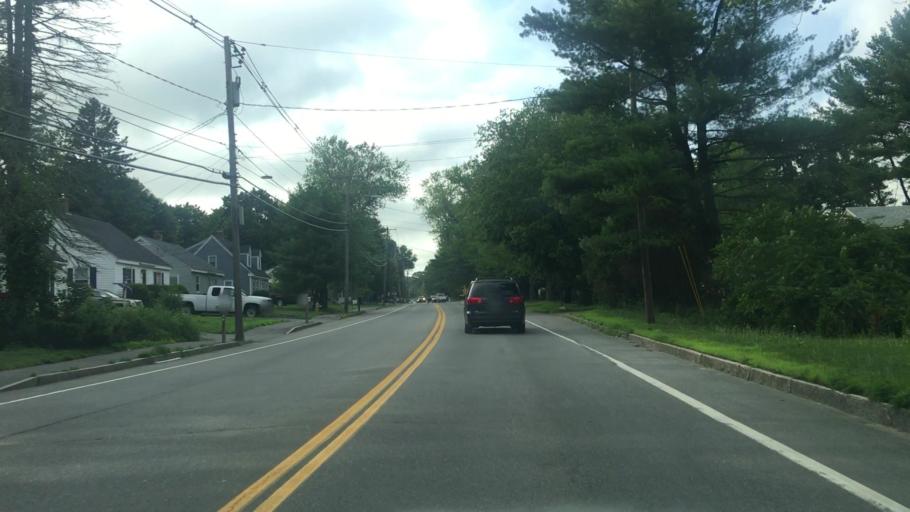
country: US
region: Maine
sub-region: Cumberland County
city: Westbrook
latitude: 43.7054
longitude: -70.3265
